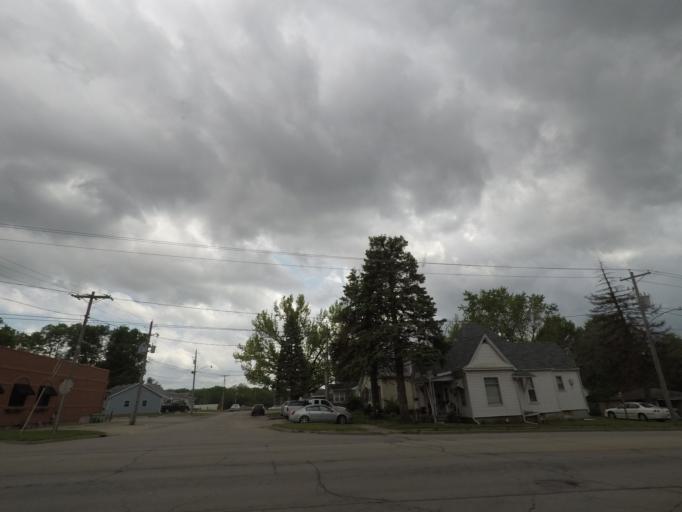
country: US
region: Illinois
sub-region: De Witt County
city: Clinton
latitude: 40.1483
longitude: -88.9604
